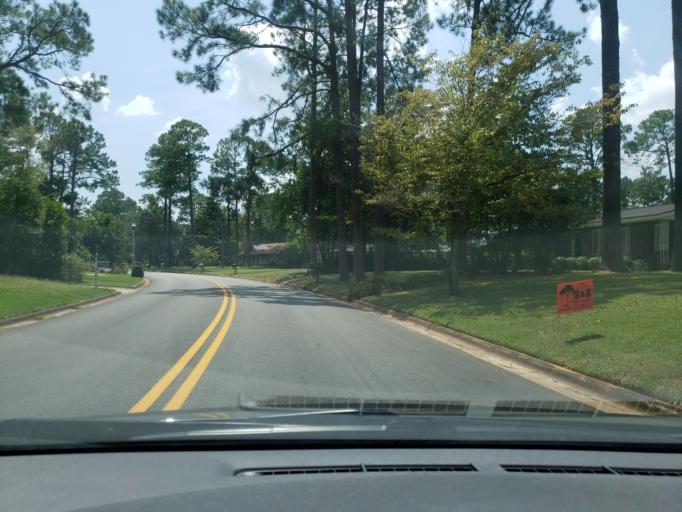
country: US
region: Georgia
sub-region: Dougherty County
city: Albany
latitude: 31.5986
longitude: -84.2052
